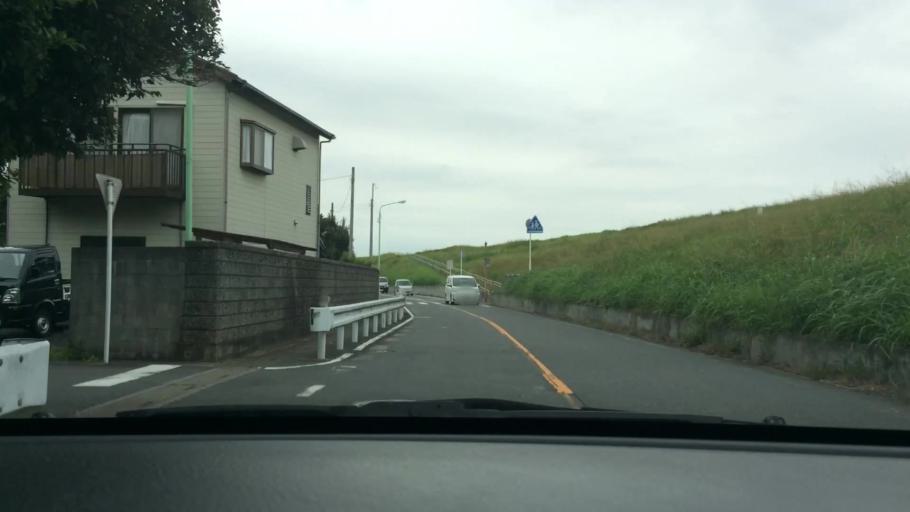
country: JP
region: Chiba
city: Matsudo
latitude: 35.8012
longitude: 139.8892
